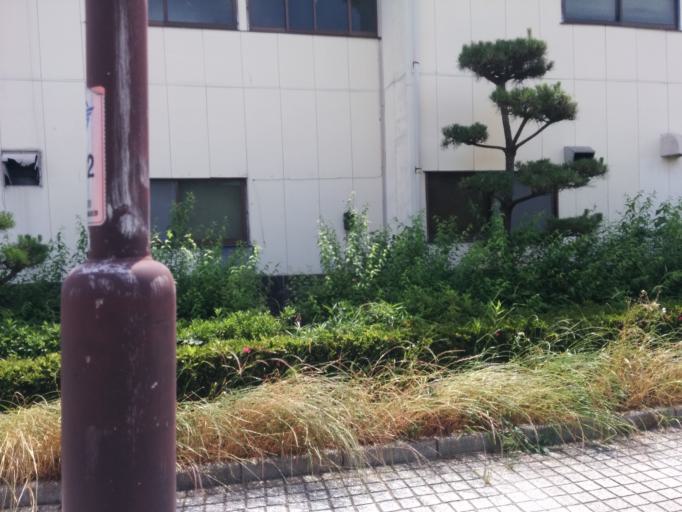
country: JP
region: Tokyo
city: Higashimurayama-shi
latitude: 35.7688
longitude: 139.4905
